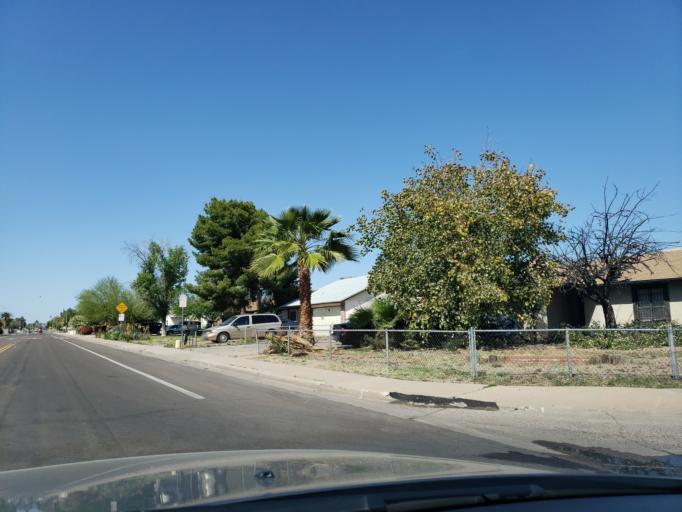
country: US
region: Arizona
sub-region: Maricopa County
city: Glendale
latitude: 33.5625
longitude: -112.1776
